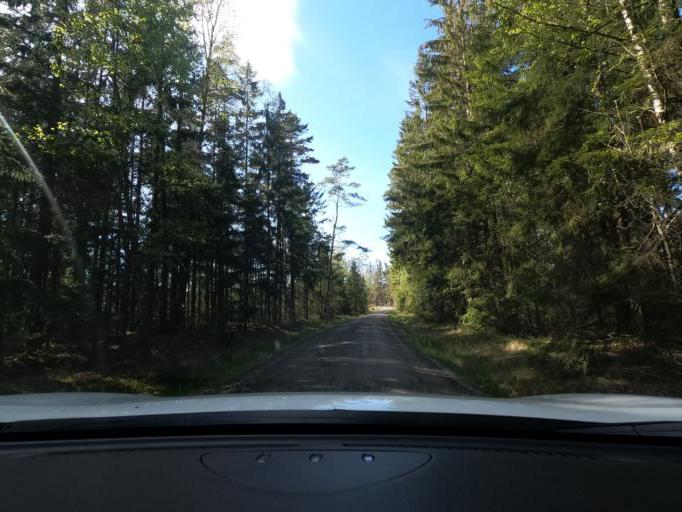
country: SE
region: Vaestra Goetaland
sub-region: Harryda Kommun
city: Ravlanda
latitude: 57.5949
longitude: 12.4782
